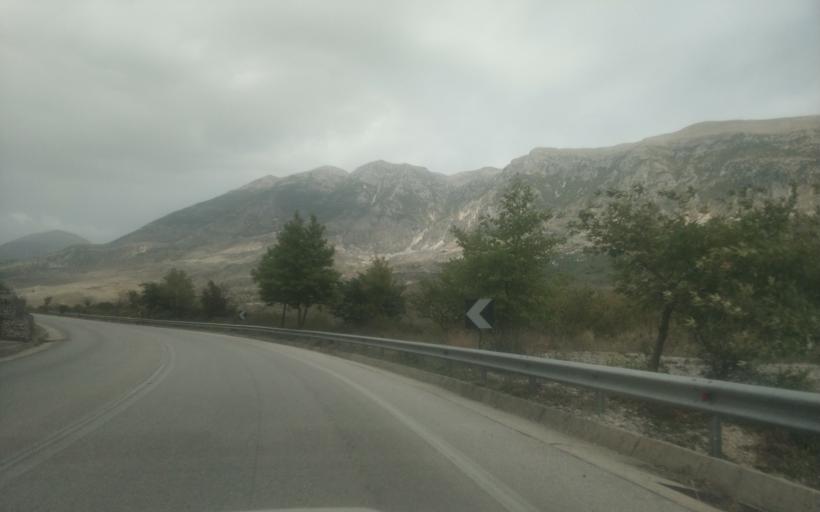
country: AL
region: Gjirokaster
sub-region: Rrethi i Gjirokastres
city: Picar
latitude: 40.2212
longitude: 20.0875
